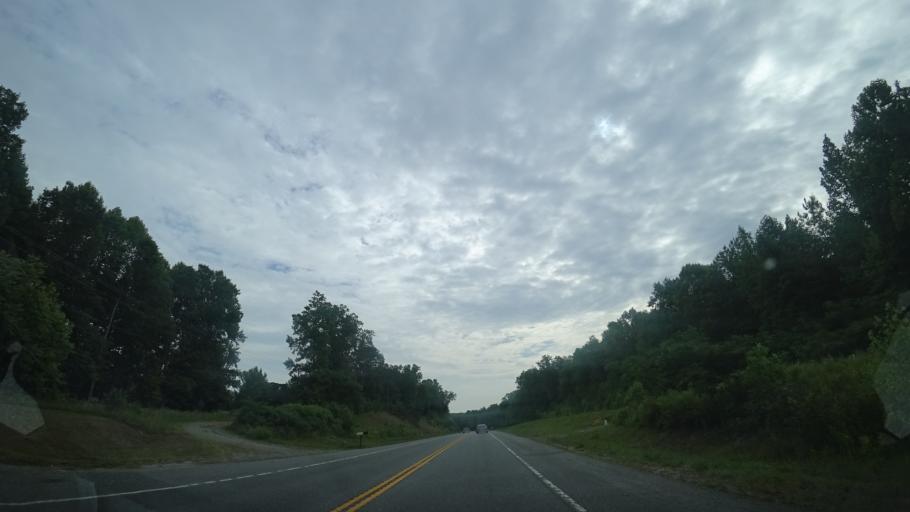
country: US
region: Virginia
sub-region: Spotsylvania County
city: Spotsylvania Courthouse
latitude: 38.1757
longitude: -77.6298
